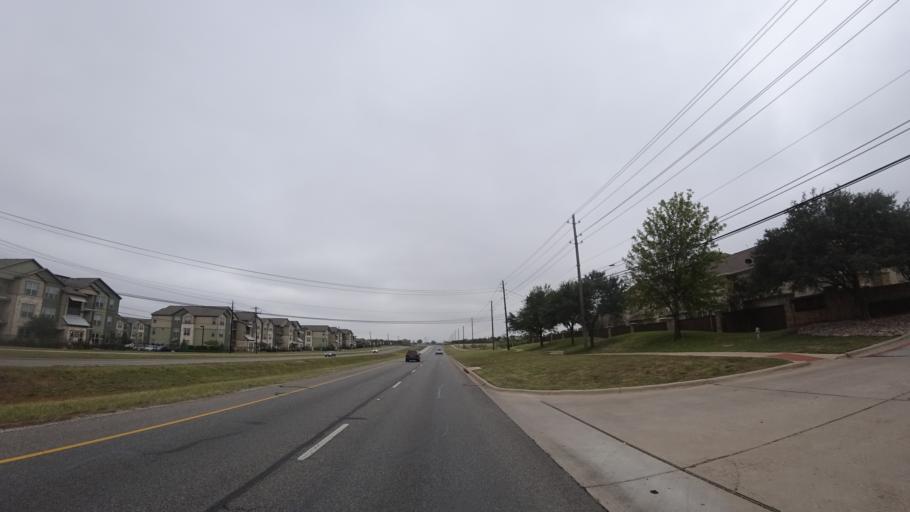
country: US
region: Texas
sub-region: Travis County
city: Pflugerville
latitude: 30.3976
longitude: -97.6546
